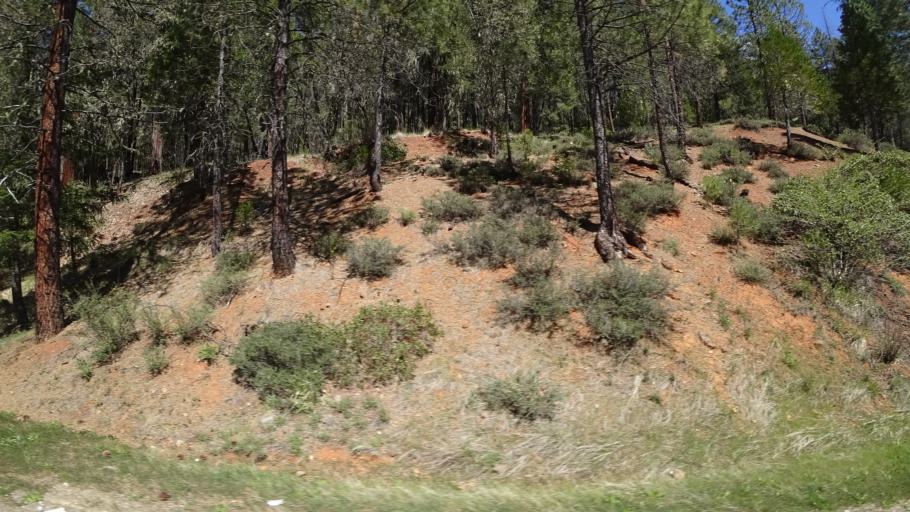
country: US
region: California
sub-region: Trinity County
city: Weaverville
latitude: 40.7692
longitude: -122.8903
